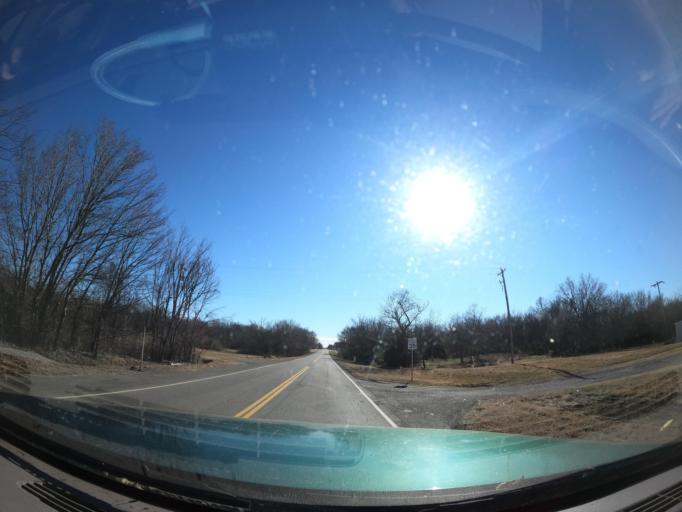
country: US
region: Oklahoma
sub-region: Muskogee County
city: Haskell
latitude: 35.6521
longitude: -95.6561
